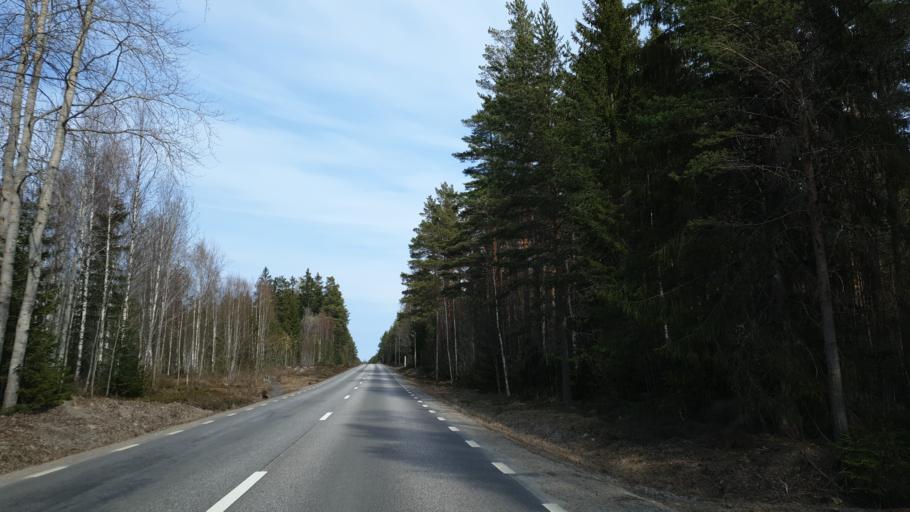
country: SE
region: Gaevleborg
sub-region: Gavle Kommun
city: Norrsundet
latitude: 61.0059
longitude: 17.1289
